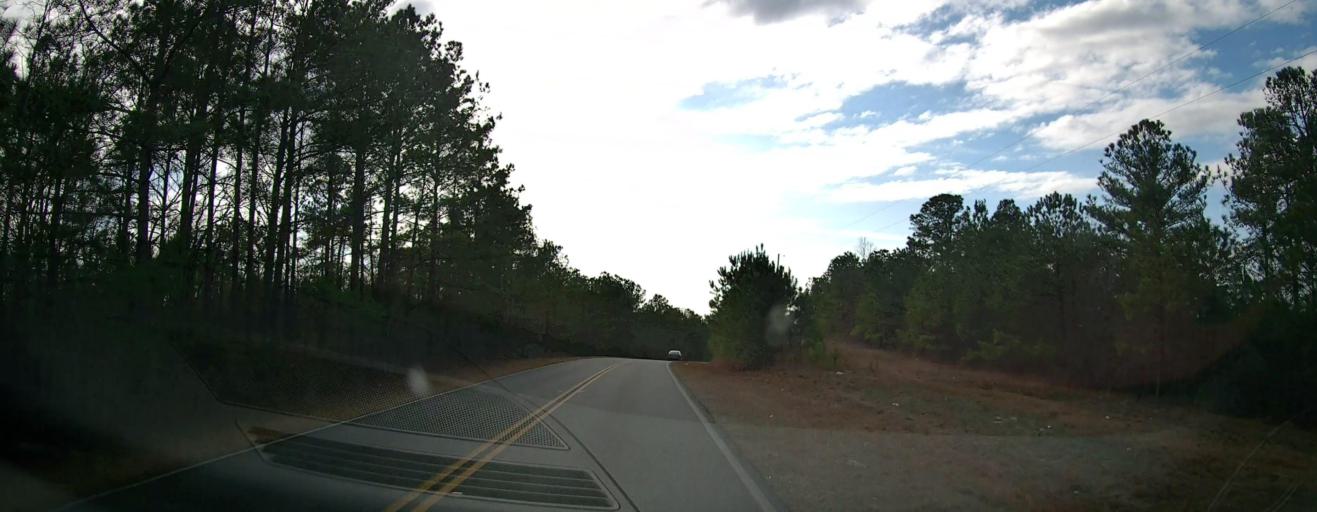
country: US
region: Georgia
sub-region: Talbot County
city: Talbotton
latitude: 32.4981
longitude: -84.5750
